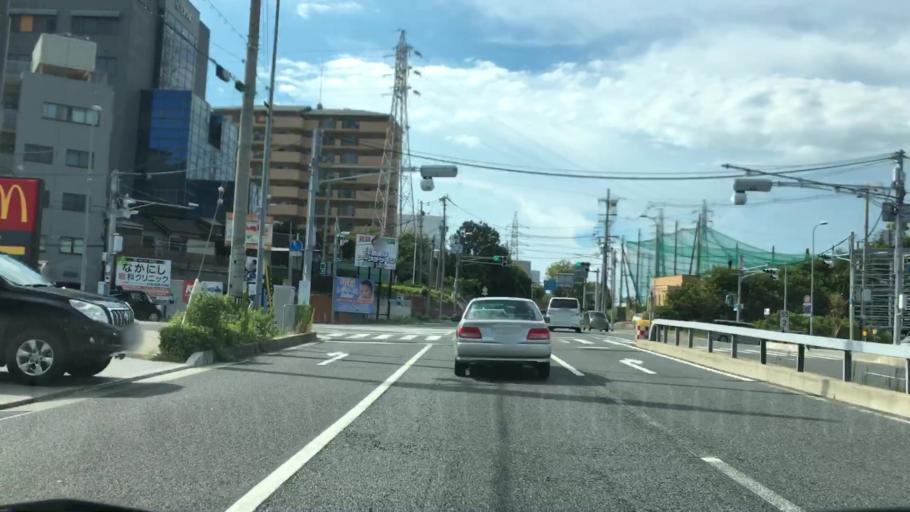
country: JP
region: Hyogo
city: Akashi
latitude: 34.6538
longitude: 134.9753
